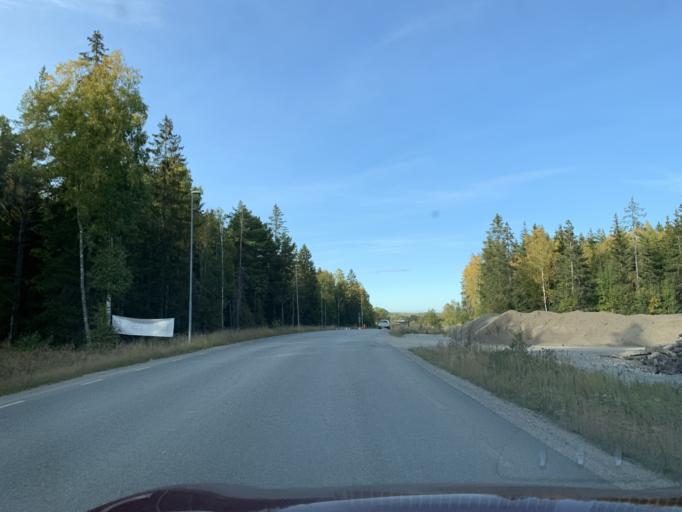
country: SE
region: Stockholm
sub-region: Upplands-Bro Kommun
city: Bro
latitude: 59.5094
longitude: 17.6153
